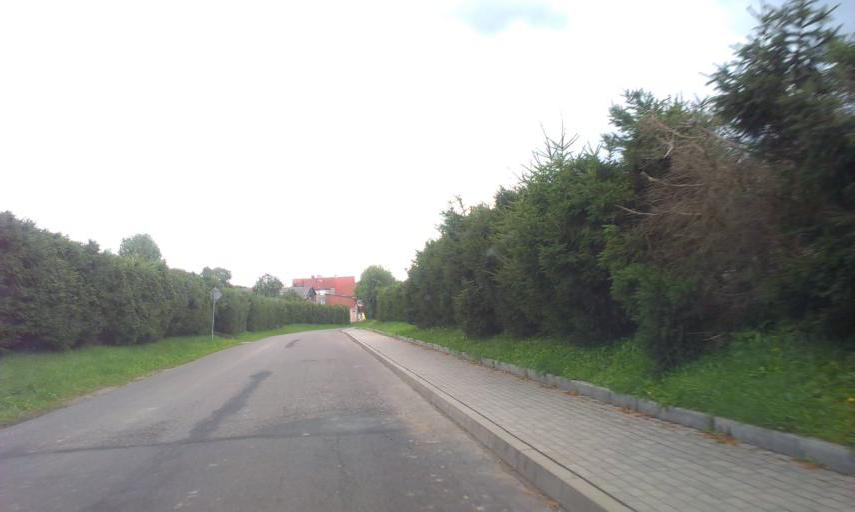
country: PL
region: West Pomeranian Voivodeship
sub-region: Powiat bialogardzki
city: Tychowo
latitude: 53.9293
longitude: 16.2549
